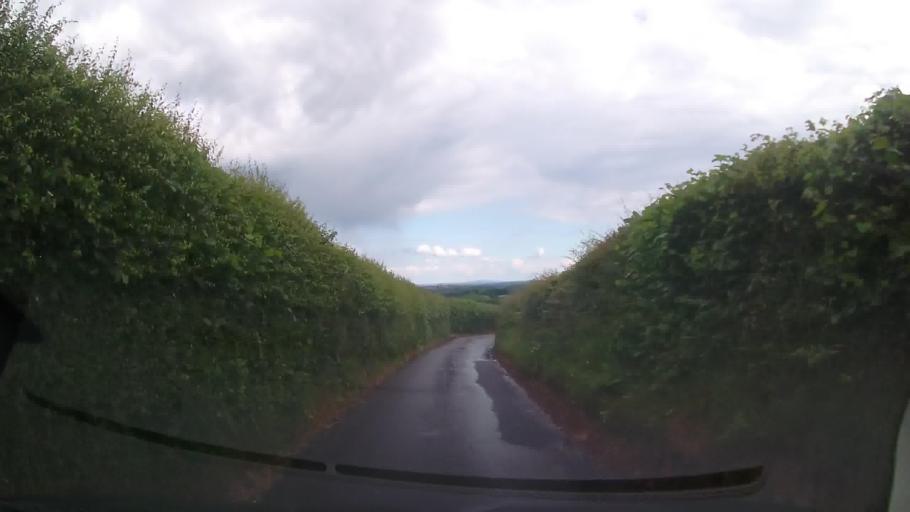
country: GB
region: England
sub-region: Telford and Wrekin
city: Ironbridge
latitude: 52.6531
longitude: -2.5137
